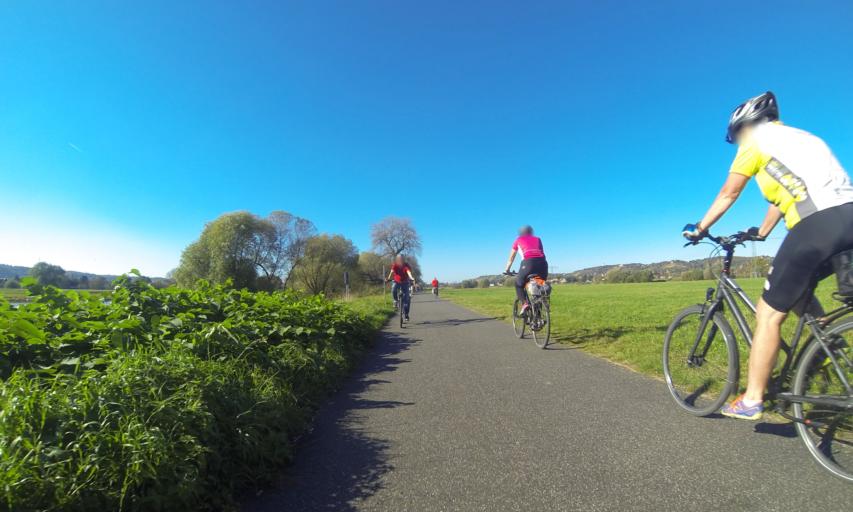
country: DE
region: Saxony
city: Radebeul
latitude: 51.0944
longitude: 13.6520
